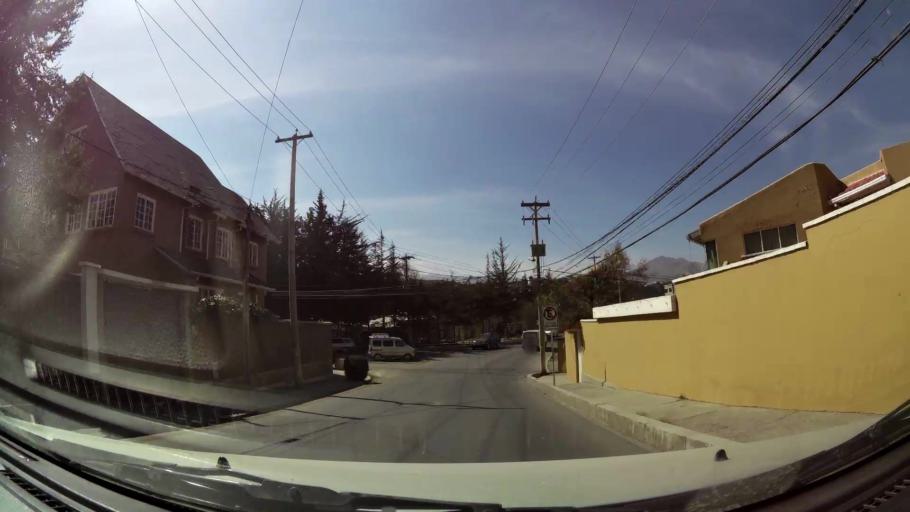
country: BO
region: La Paz
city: La Paz
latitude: -16.5256
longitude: -68.0906
